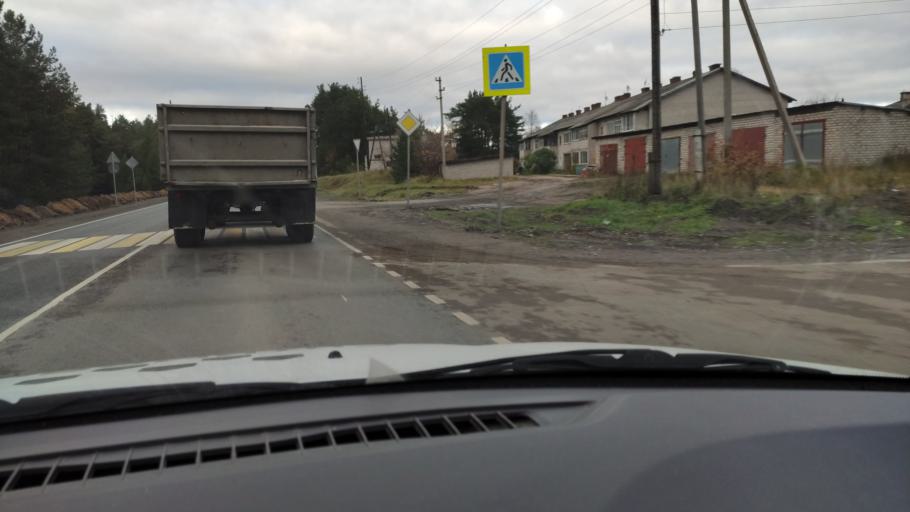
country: RU
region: Kirov
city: Belaya Kholunitsa
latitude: 58.8499
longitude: 50.8282
